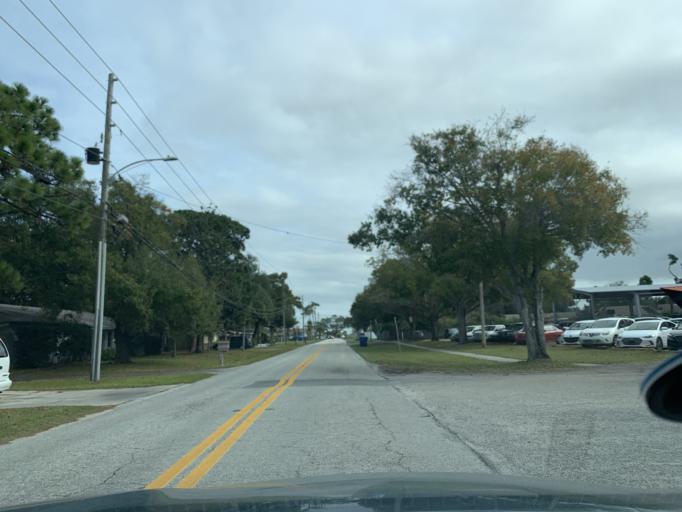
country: US
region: Florida
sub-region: Pinellas County
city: Ridgecrest
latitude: 27.8874
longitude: -82.7904
